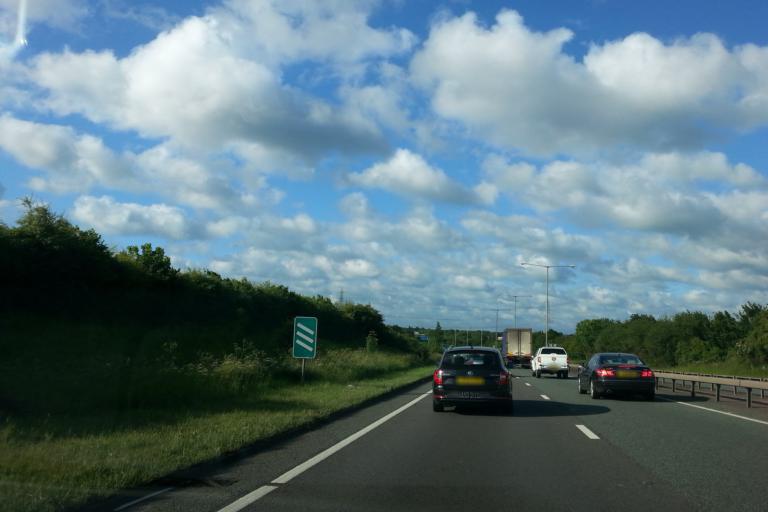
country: GB
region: England
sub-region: Leicestershire
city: Kirby Muxloe
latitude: 52.6517
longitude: -1.2208
